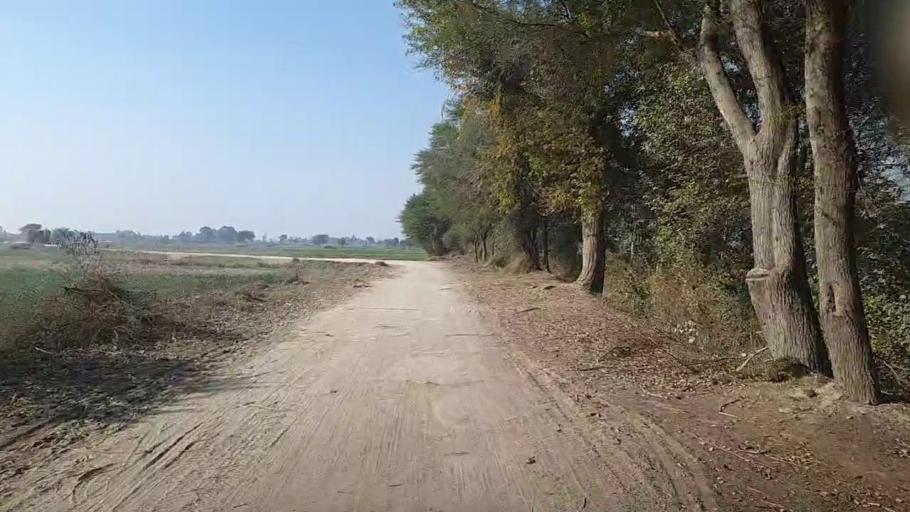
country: PK
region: Sindh
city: Mirpur Mathelo
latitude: 27.8985
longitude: 69.6496
